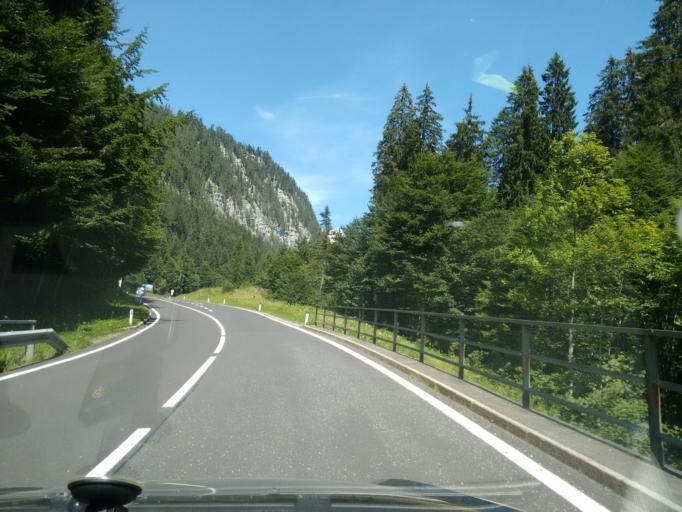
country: AT
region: Styria
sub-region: Politischer Bezirk Liezen
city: Ardning
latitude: 47.6128
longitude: 14.2910
